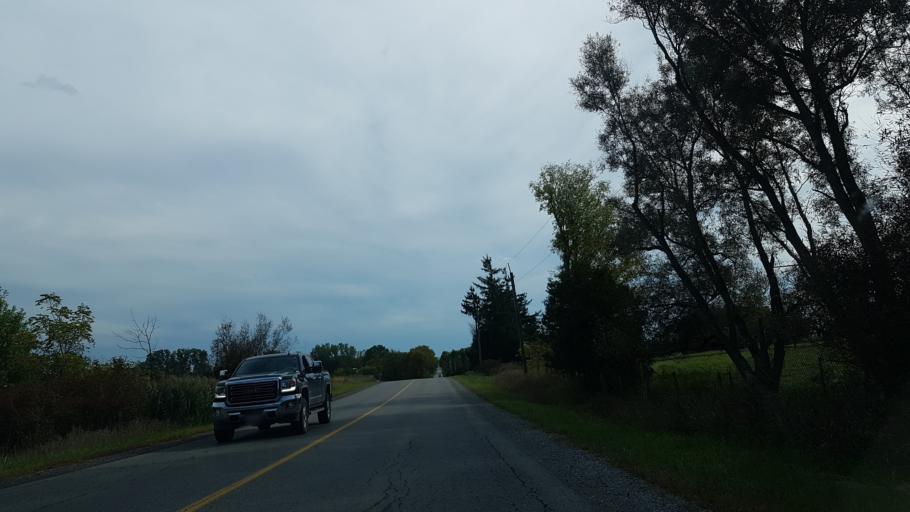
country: CA
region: Ontario
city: Delaware
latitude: 43.0121
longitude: -81.4021
